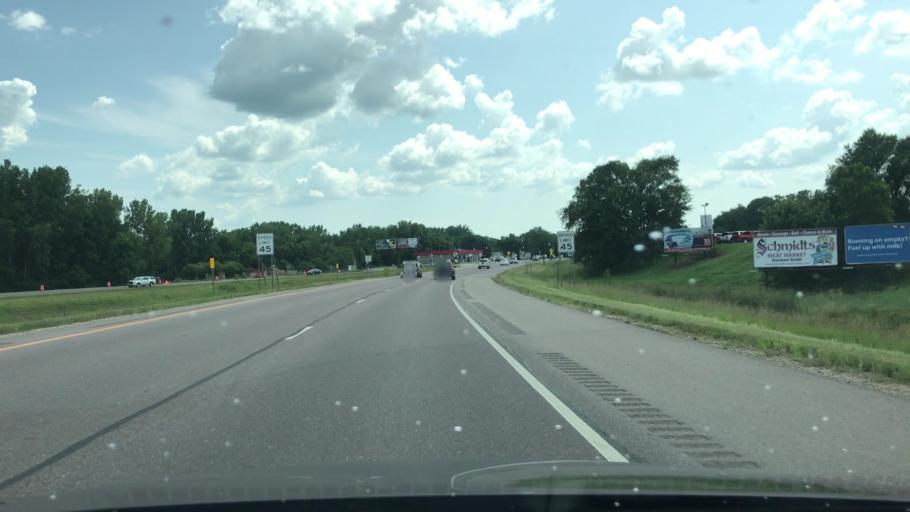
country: US
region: Minnesota
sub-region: Nicollet County
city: Saint Peter
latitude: 44.3358
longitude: -93.9483
